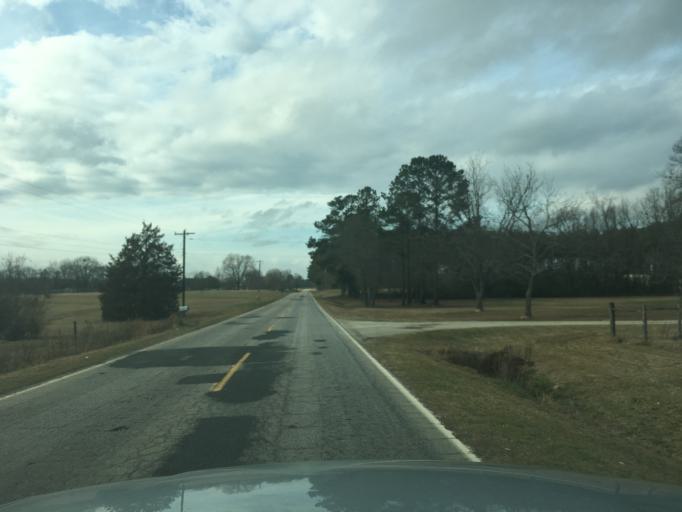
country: US
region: South Carolina
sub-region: Abbeville County
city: Due West
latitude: 34.3317
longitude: -82.4808
